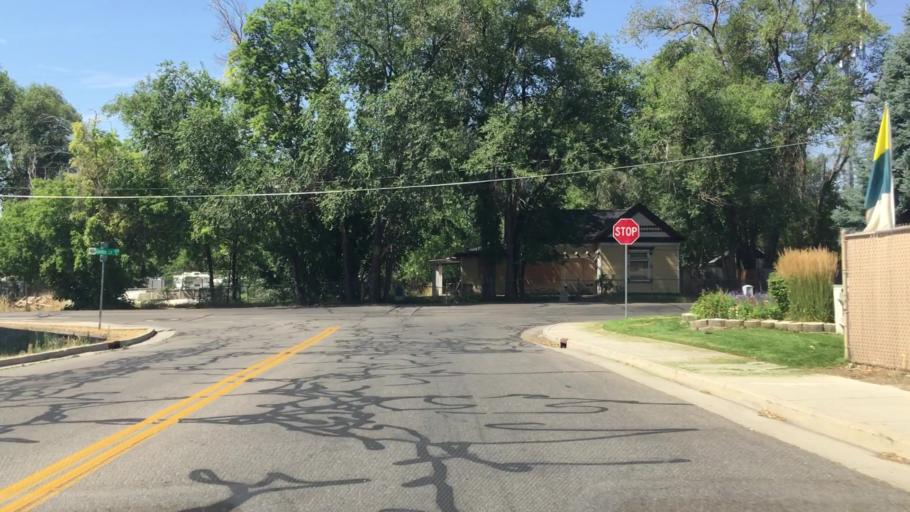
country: US
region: Utah
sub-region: Salt Lake County
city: Millcreek
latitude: 40.6792
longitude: -111.8840
